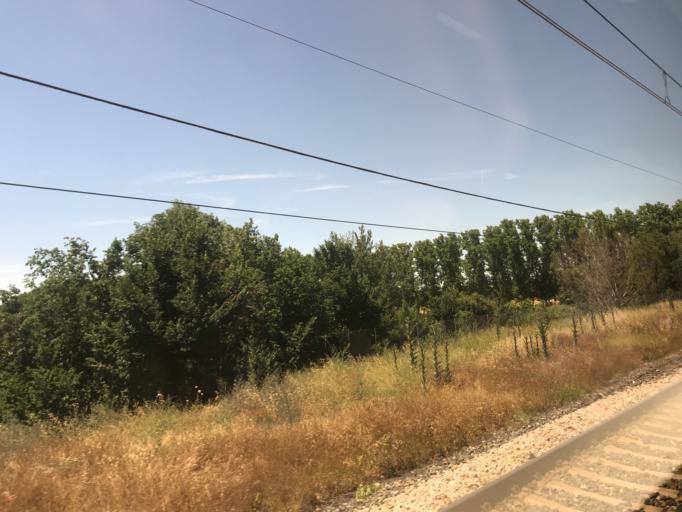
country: ES
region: Madrid
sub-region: Provincia de Madrid
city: Aranjuez
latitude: 40.0402
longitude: -3.6205
